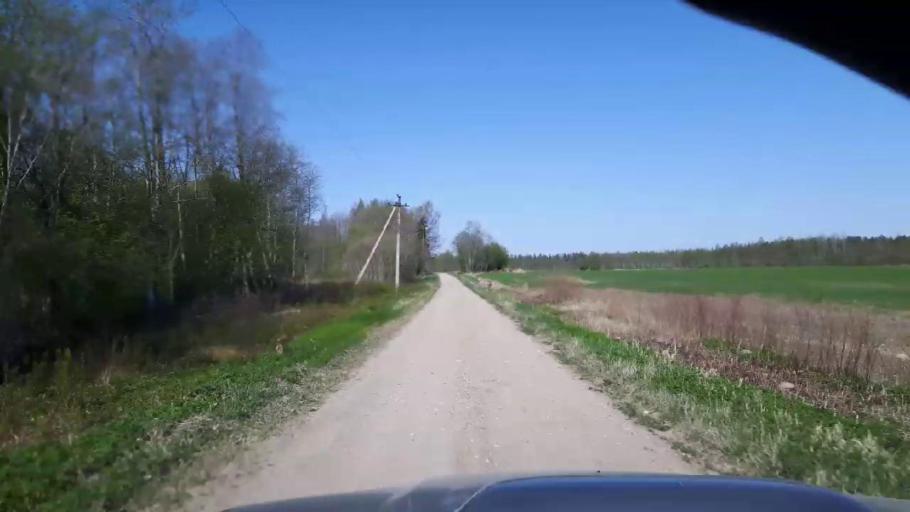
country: EE
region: Paernumaa
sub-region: Tootsi vald
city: Tootsi
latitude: 58.4457
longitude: 24.8068
